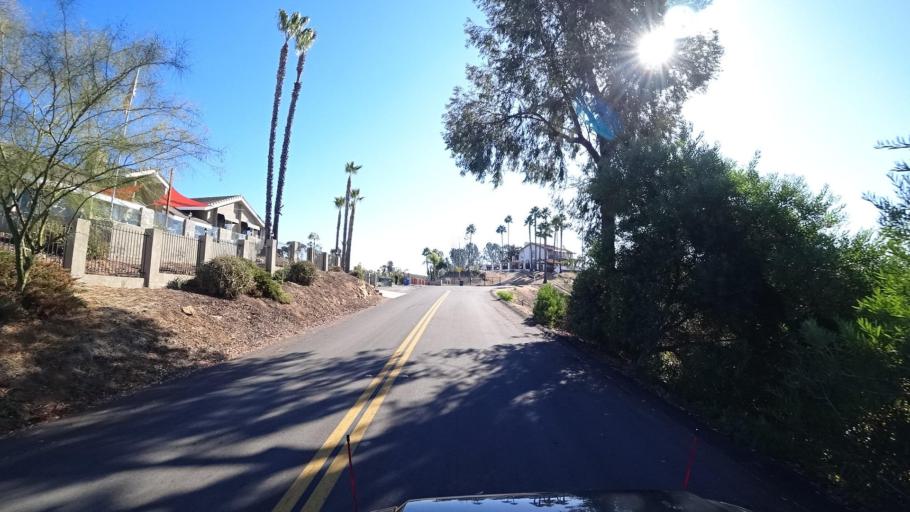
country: US
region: California
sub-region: San Diego County
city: Winter Gardens
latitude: 32.8310
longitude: -116.9262
